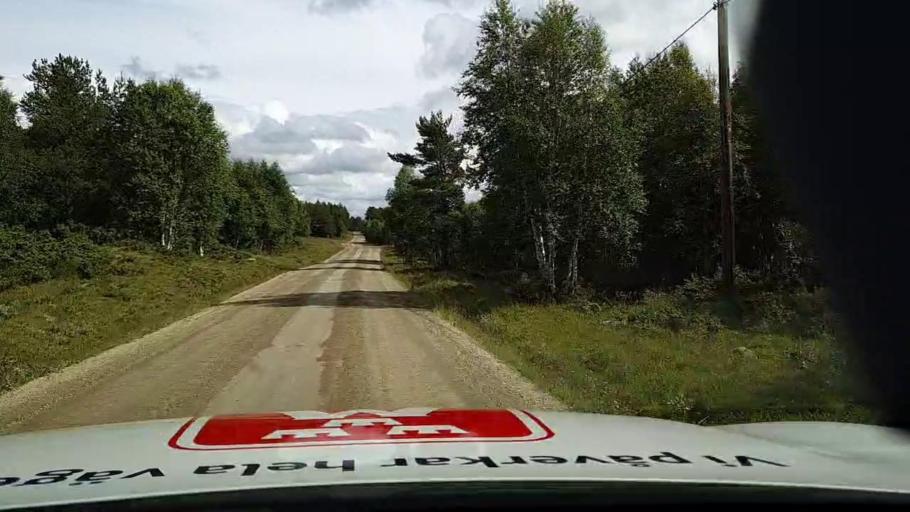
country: SE
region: Jaemtland
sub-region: Are Kommun
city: Jarpen
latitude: 62.5520
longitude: 13.4433
